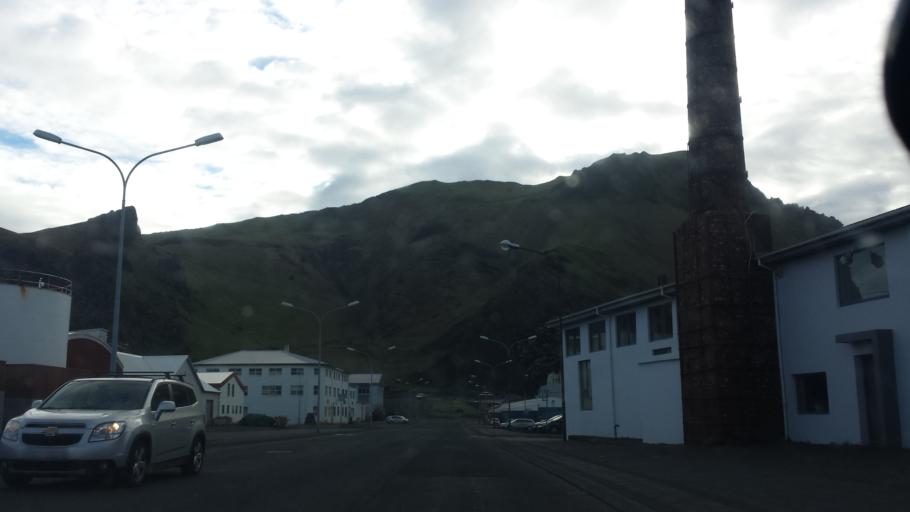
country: IS
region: South
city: Vestmannaeyjar
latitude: 63.4429
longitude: -20.2774
